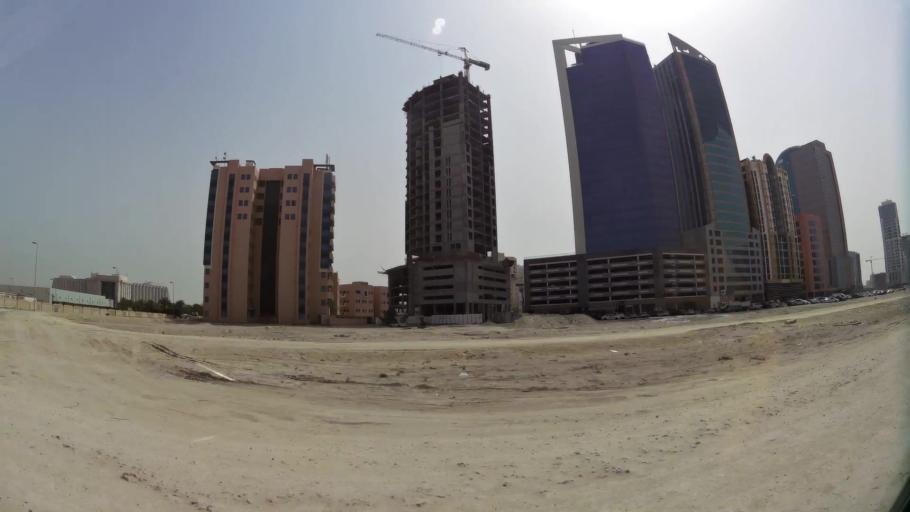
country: BH
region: Manama
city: Jidd Hafs
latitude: 26.2419
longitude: 50.5348
